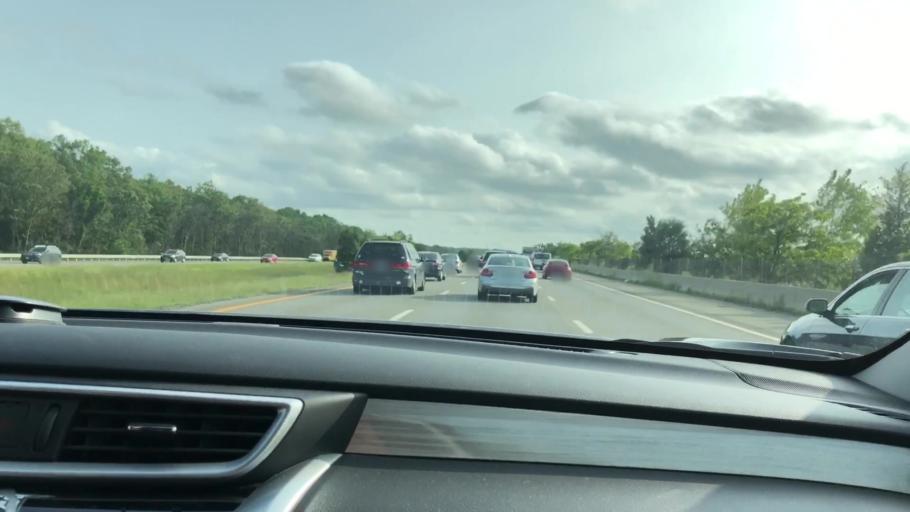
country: US
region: Massachusetts
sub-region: Bristol County
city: Attleboro
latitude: 41.9469
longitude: -71.3101
